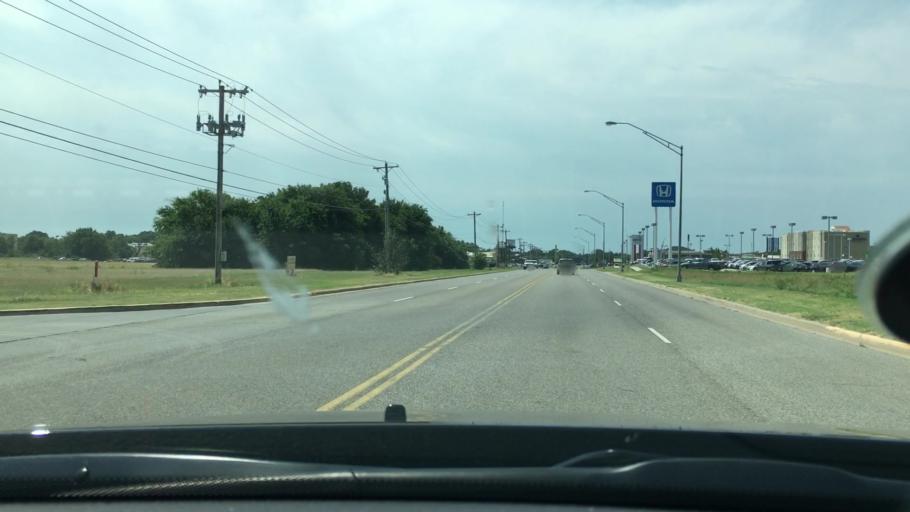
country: US
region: Oklahoma
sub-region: Carter County
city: Ardmore
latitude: 34.1939
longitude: -97.1605
